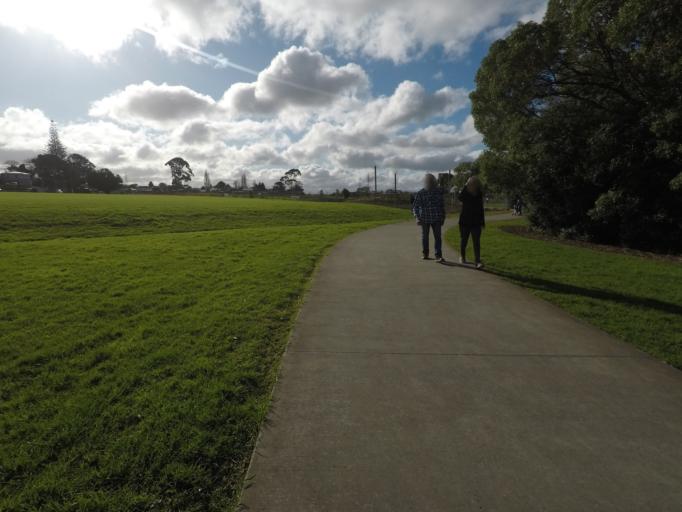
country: NZ
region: Auckland
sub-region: Auckland
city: Rosebank
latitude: -36.8947
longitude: 174.6714
